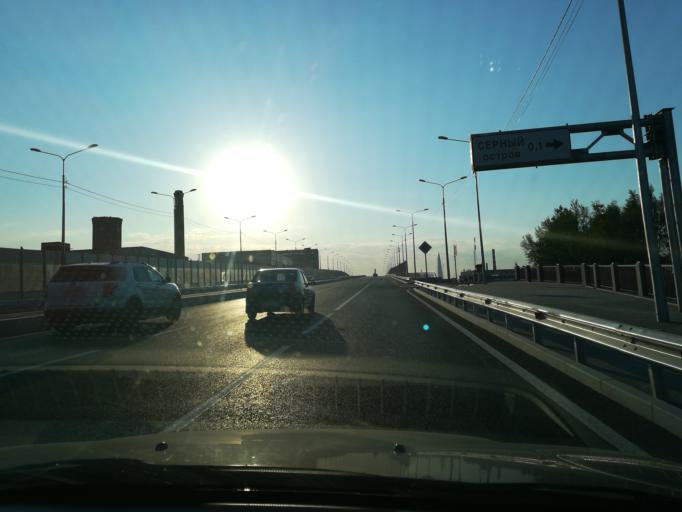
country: RU
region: Leningrad
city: Krestovskiy ostrov
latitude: 59.9549
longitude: 30.2637
